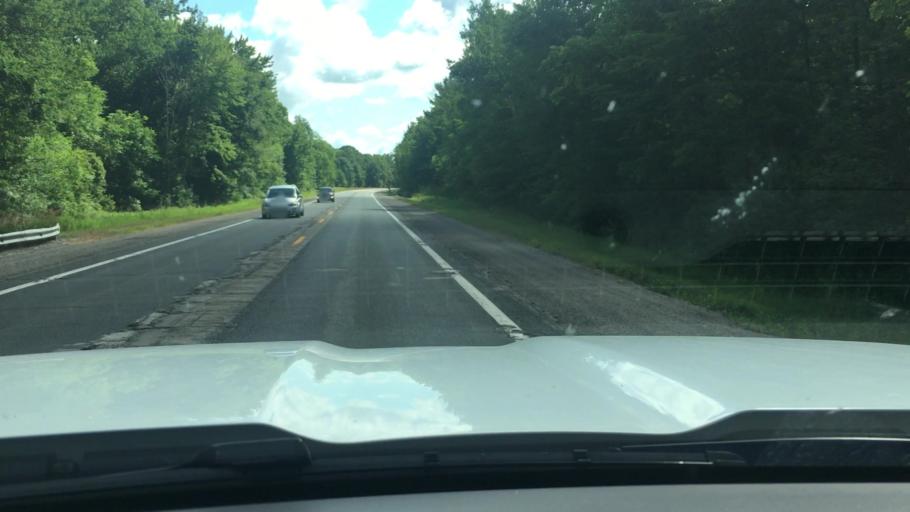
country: US
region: Michigan
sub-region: Clinton County
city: Ovid
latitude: 43.1851
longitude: -84.3338
